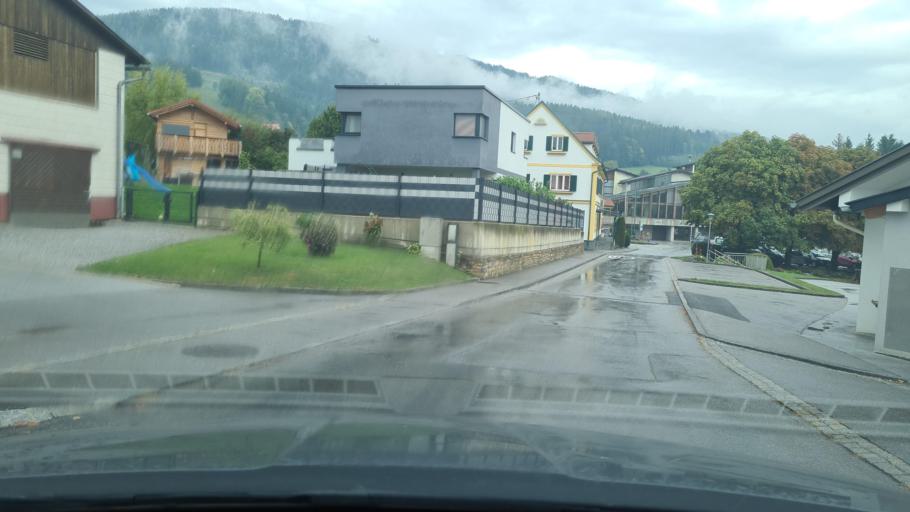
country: AT
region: Styria
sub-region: Politischer Bezirk Weiz
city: Passail
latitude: 47.2848
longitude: 15.4761
